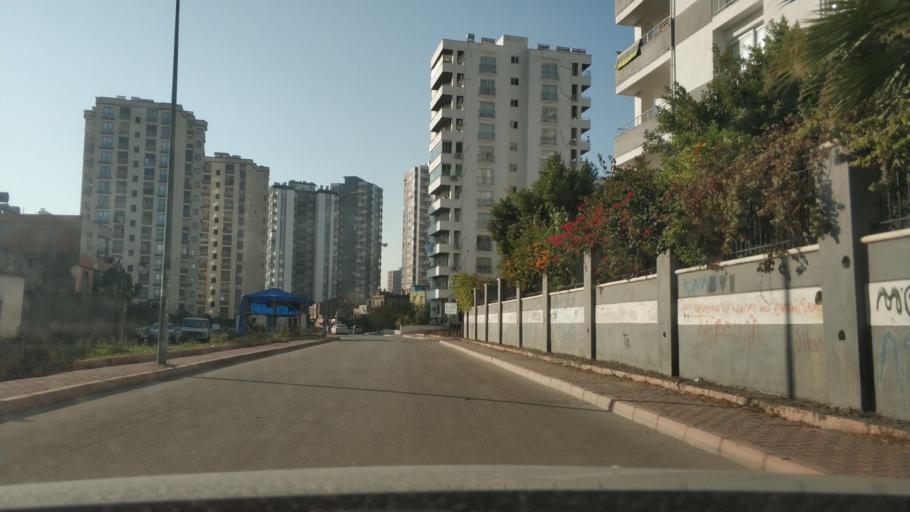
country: TR
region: Adana
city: Seyhan
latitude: 37.0148
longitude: 35.2899
